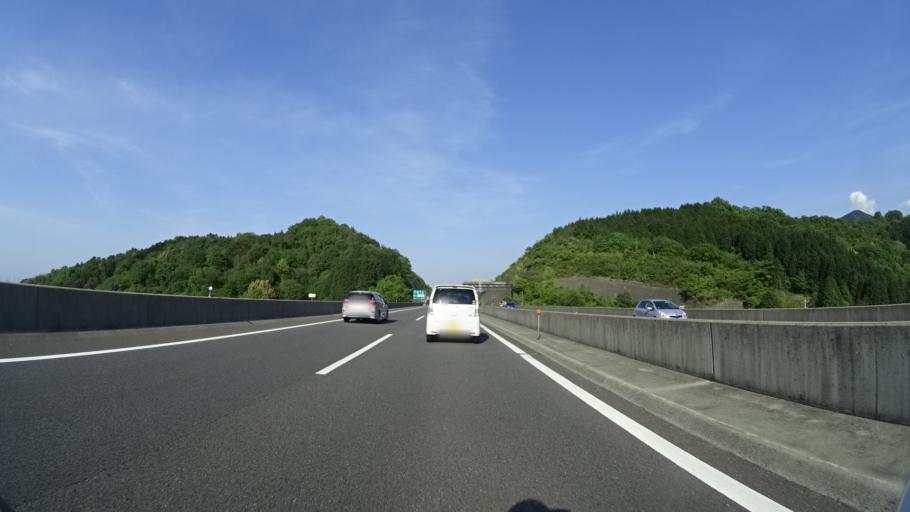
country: JP
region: Ehime
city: Saijo
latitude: 33.8849
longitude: 133.0972
